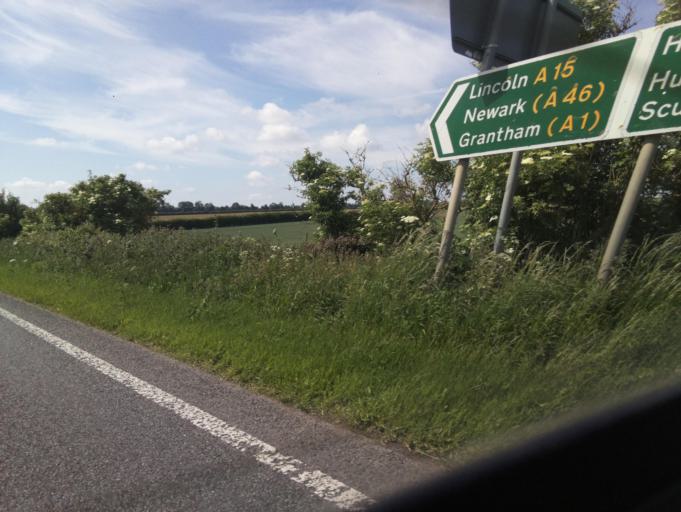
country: GB
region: England
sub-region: Lincolnshire
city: Burton
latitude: 53.2691
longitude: -0.5395
